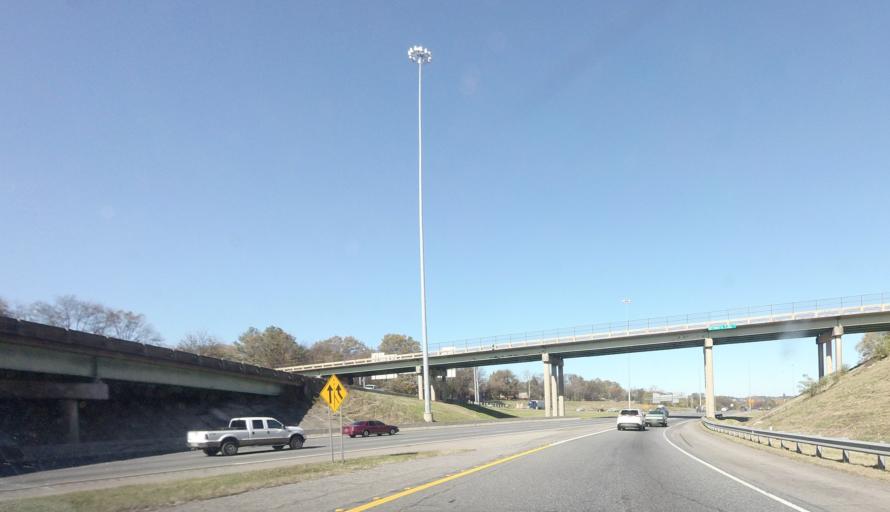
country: US
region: Alabama
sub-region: Jefferson County
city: Birmingham
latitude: 33.5240
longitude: -86.8268
